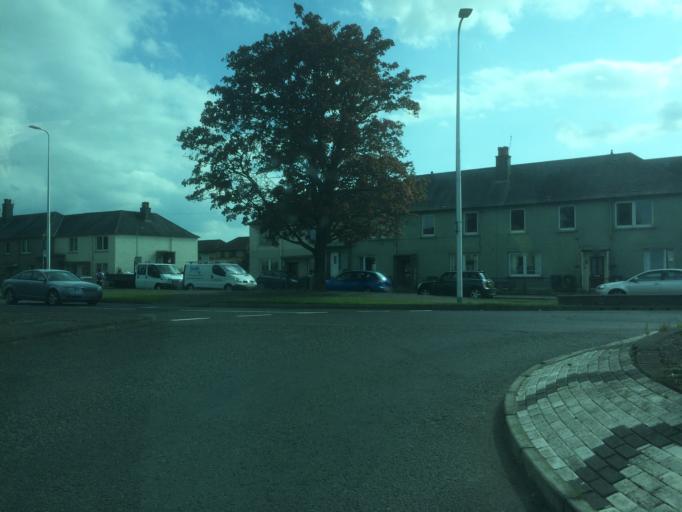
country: GB
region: Scotland
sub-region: Perth and Kinross
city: Perth
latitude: 56.4088
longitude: -3.4501
